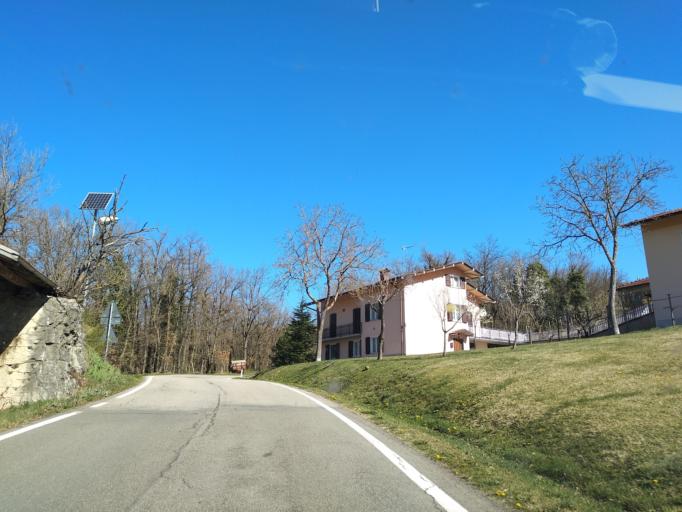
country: IT
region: Emilia-Romagna
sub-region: Provincia di Reggio Emilia
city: Castelnovo ne'Monti
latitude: 44.4017
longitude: 10.3973
